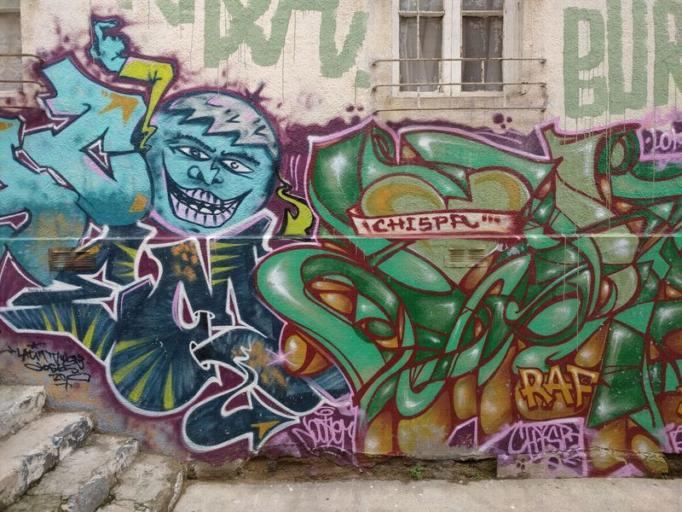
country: CL
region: Valparaiso
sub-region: Provincia de Valparaiso
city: Valparaiso
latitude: -33.0477
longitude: -71.6222
